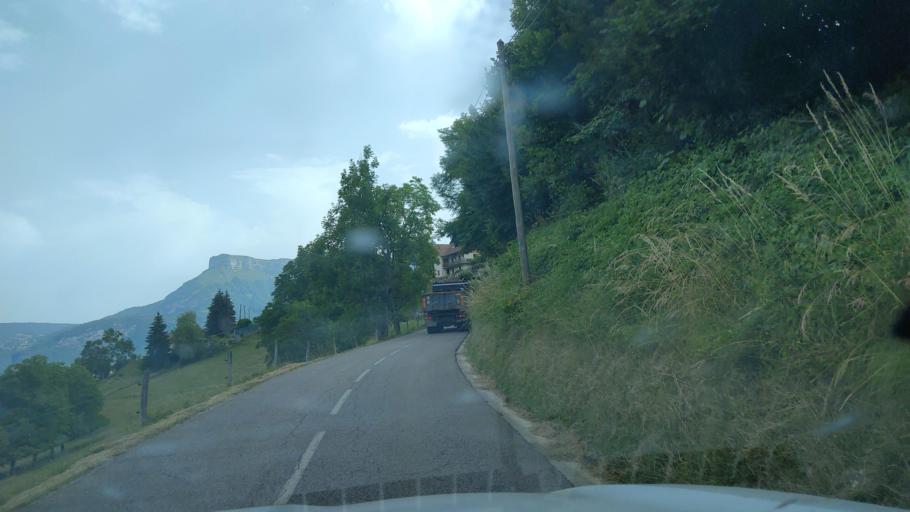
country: FR
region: Rhone-Alpes
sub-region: Departement de la Savoie
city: Barby
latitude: 45.5690
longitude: 6.0255
